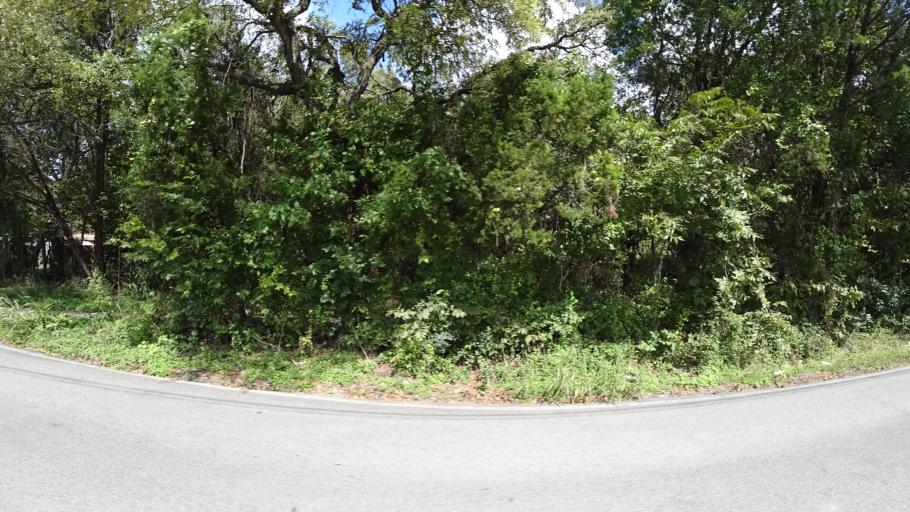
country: US
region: Texas
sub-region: Travis County
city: Onion Creek
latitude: 30.1829
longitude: -97.7848
